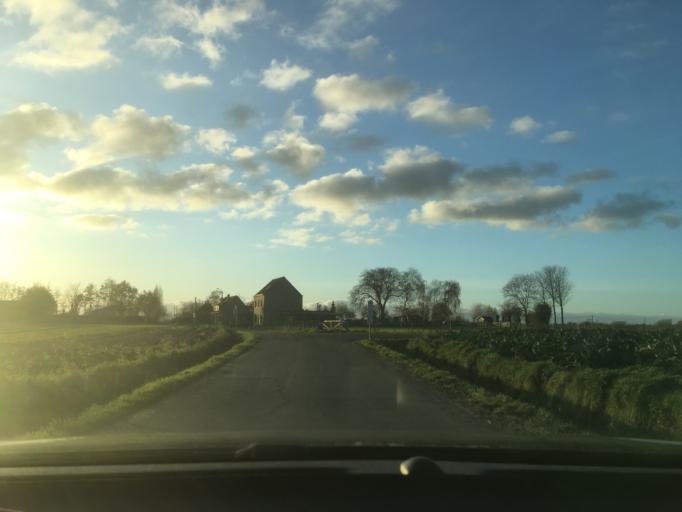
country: BE
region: Flanders
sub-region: Provincie West-Vlaanderen
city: Menen
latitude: 50.8248
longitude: 3.1093
